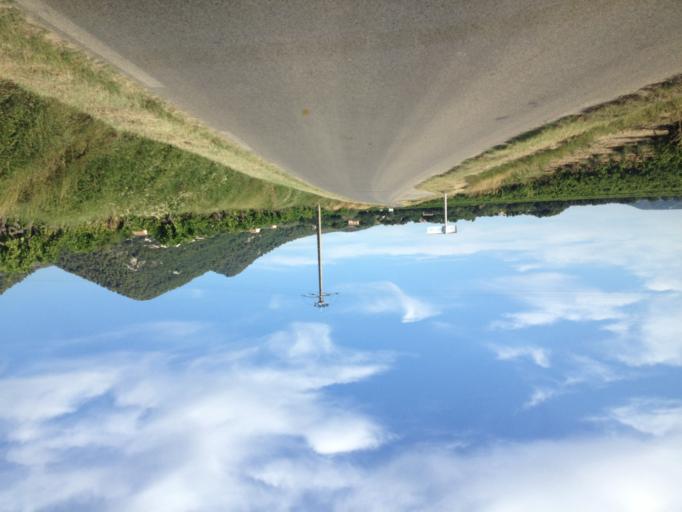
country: FR
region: Provence-Alpes-Cote d'Azur
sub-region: Departement du Vaucluse
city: Sablet
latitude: 44.1982
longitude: 5.0101
